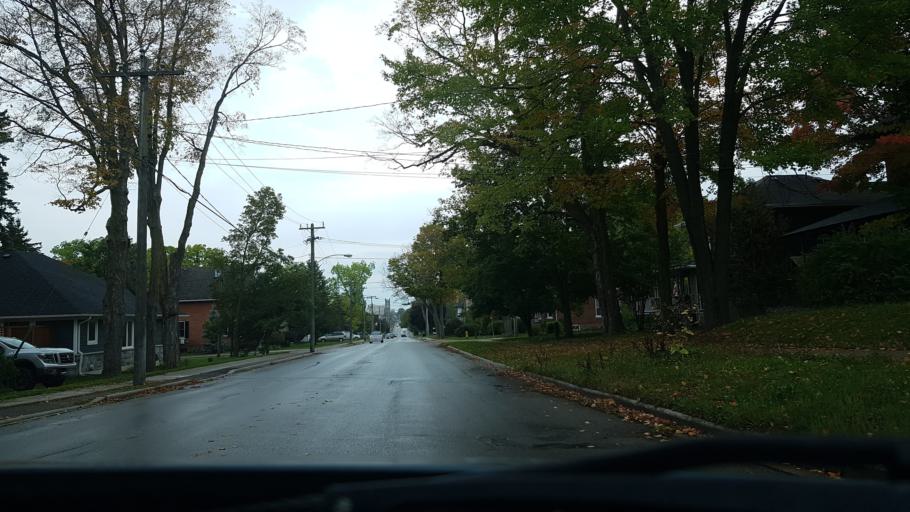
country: CA
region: Ontario
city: Omemee
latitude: 44.3626
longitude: -78.7406
